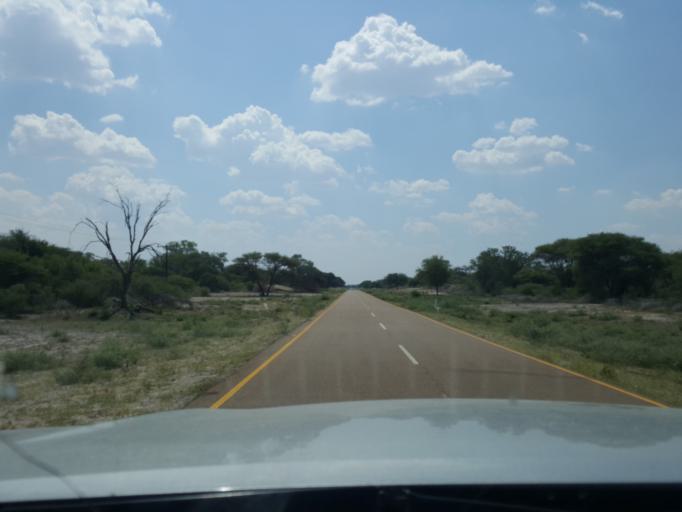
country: BW
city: Nokaneng
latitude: -19.8227
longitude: 22.2233
